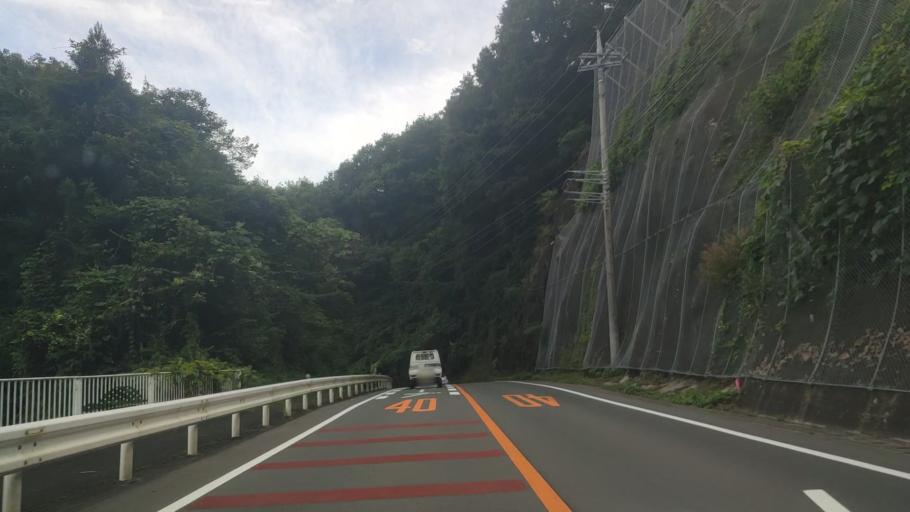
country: JP
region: Gunma
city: Omamacho-omama
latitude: 36.5440
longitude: 139.3690
